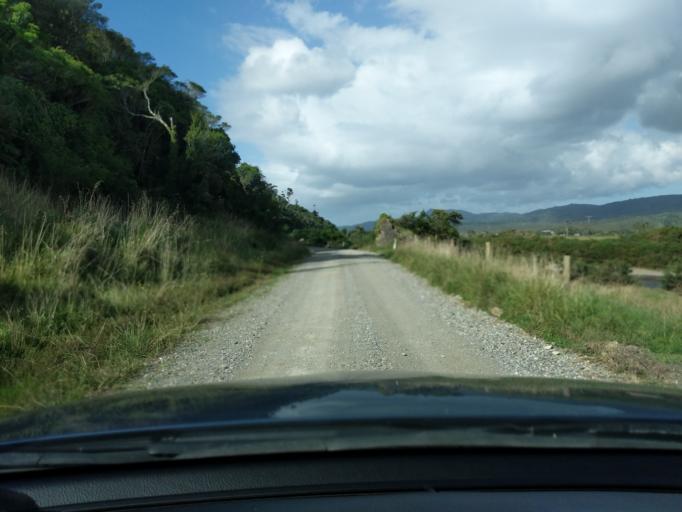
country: NZ
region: Tasman
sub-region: Tasman District
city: Takaka
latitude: -40.6537
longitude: 172.4574
